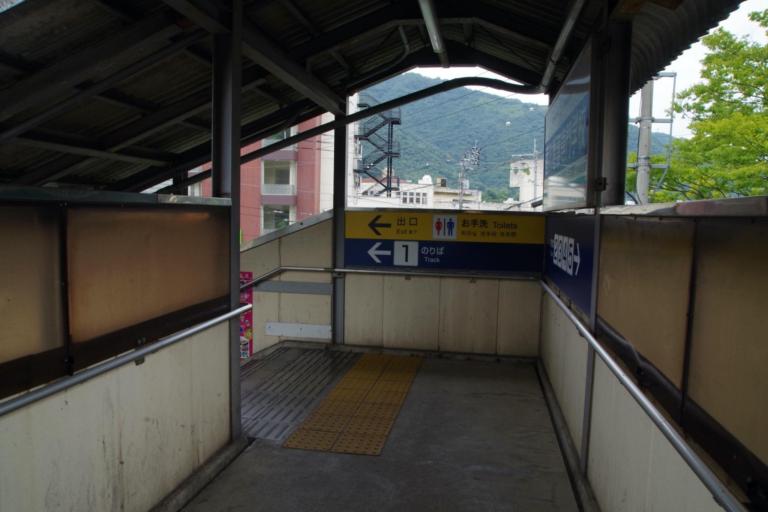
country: JP
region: Tokushima
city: Ikedacho
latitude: 34.0269
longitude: 133.8049
